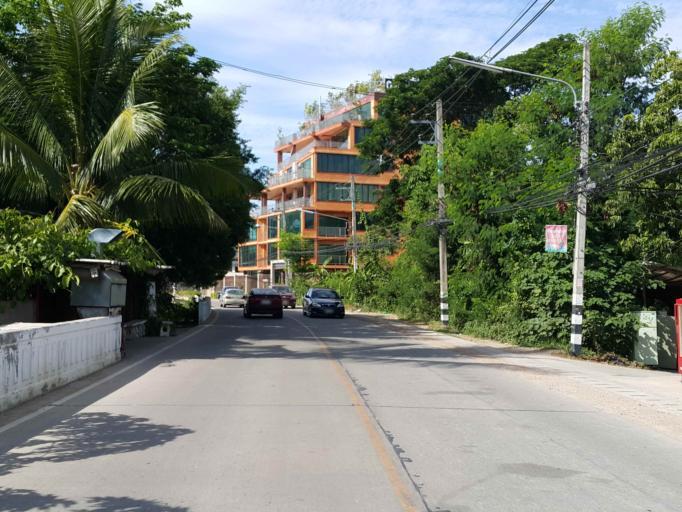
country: TH
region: Chiang Mai
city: Chiang Mai
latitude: 18.7520
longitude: 98.9876
